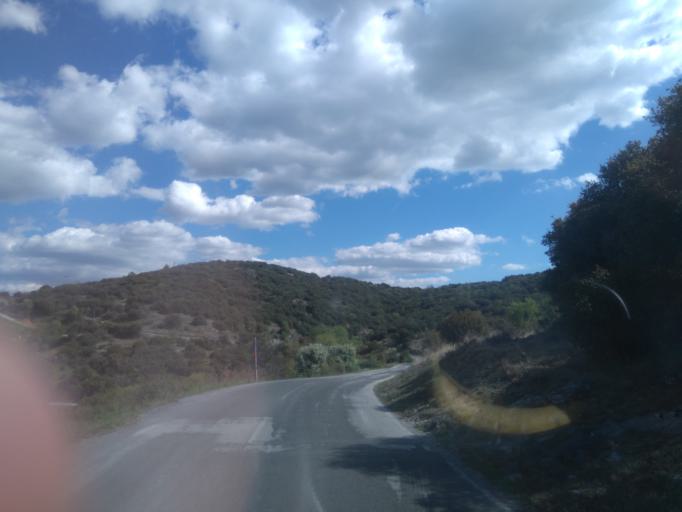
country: GR
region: Central Macedonia
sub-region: Nomos Thessalonikis
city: Asvestochori
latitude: 40.6389
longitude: 23.0142
